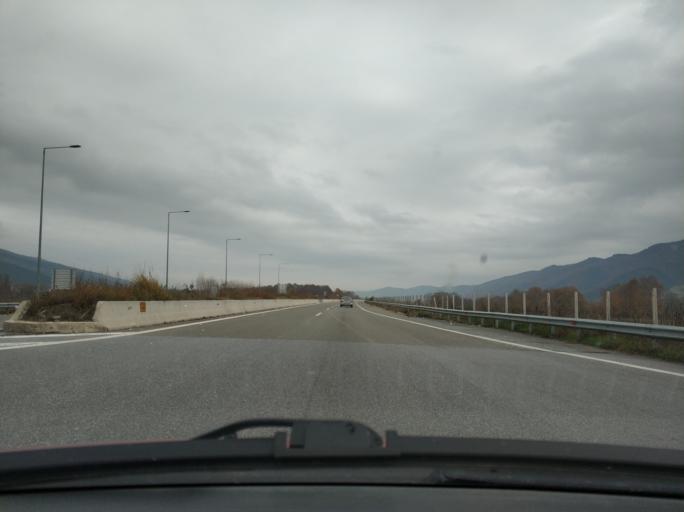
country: GR
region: East Macedonia and Thrace
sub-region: Nomos Kavalas
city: Palaiochori
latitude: 40.8583
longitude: 24.1628
